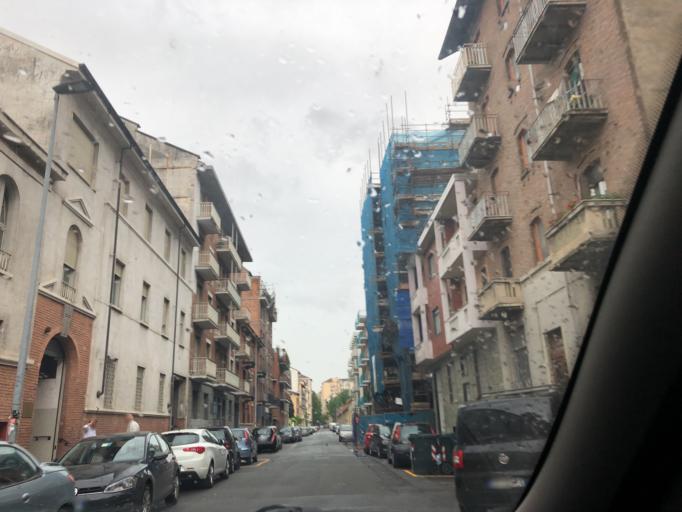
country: IT
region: Piedmont
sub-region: Provincia di Torino
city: Lesna
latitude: 45.0790
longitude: 7.6468
